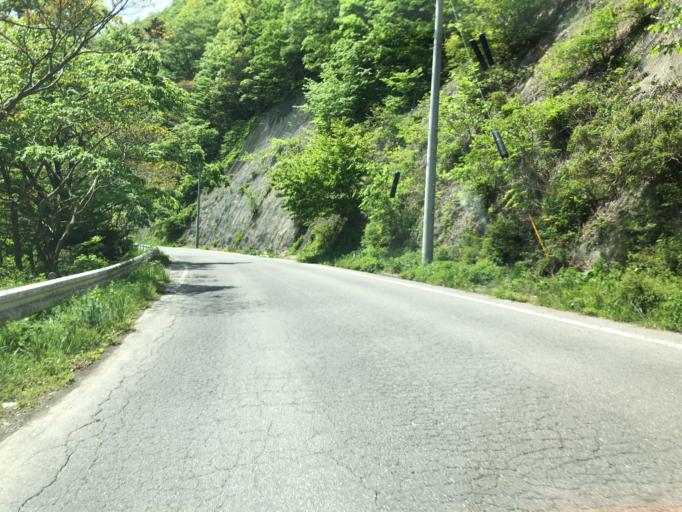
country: JP
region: Miyagi
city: Marumori
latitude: 37.7191
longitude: 140.8505
